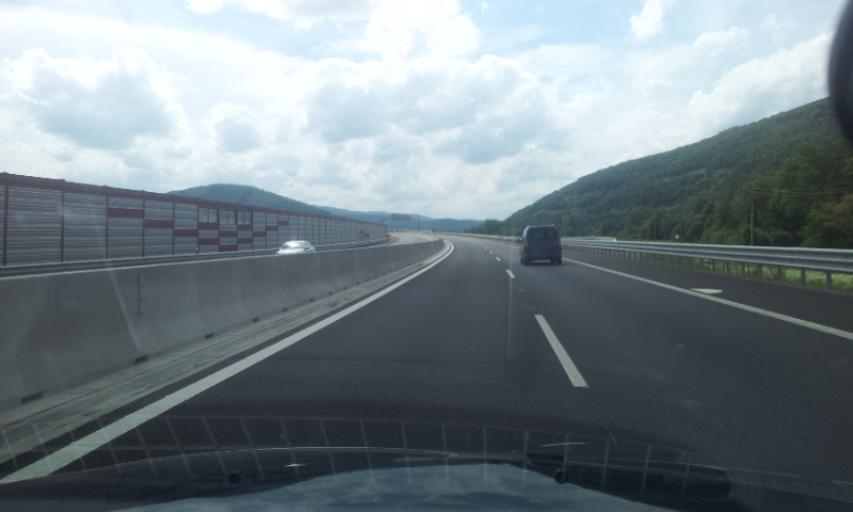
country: SK
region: Banskobystricky
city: Detva
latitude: 48.5412
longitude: 19.3864
